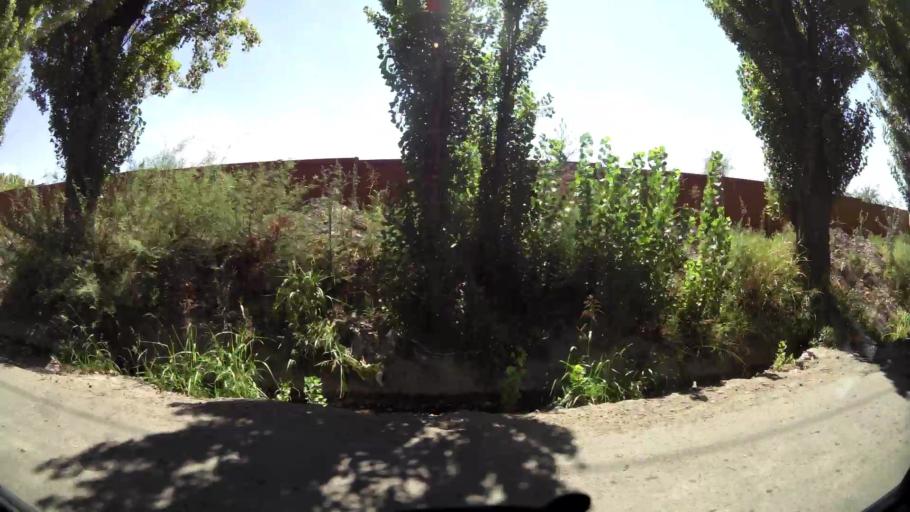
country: AR
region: Mendoza
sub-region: Departamento de Godoy Cruz
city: Godoy Cruz
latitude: -32.9768
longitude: -68.8408
